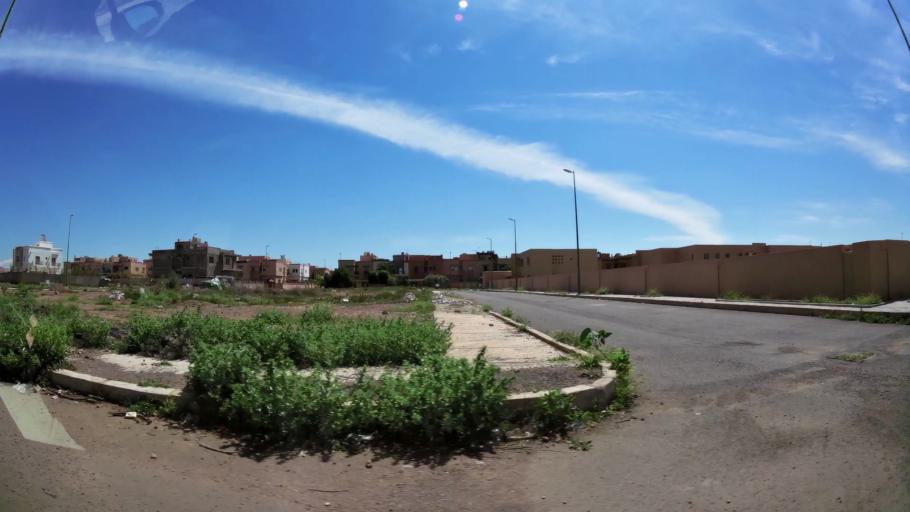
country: MA
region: Marrakech-Tensift-Al Haouz
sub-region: Marrakech
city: Marrakesh
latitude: 31.6540
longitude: -8.0769
